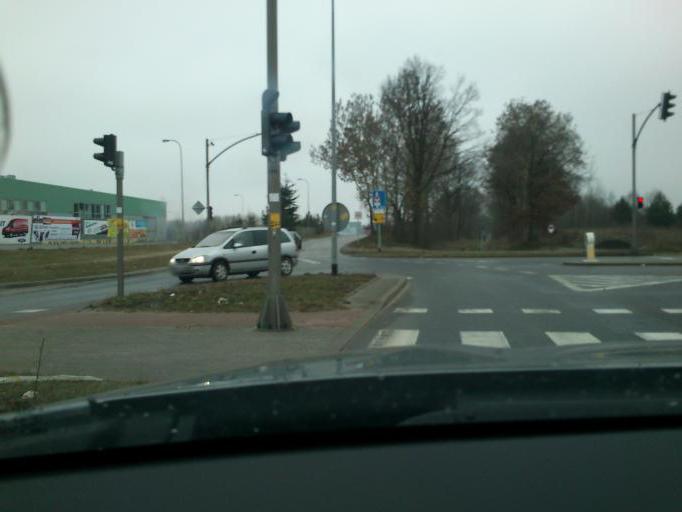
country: PL
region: Pomeranian Voivodeship
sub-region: Gdynia
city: Wielki Kack
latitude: 54.4142
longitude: 18.4805
